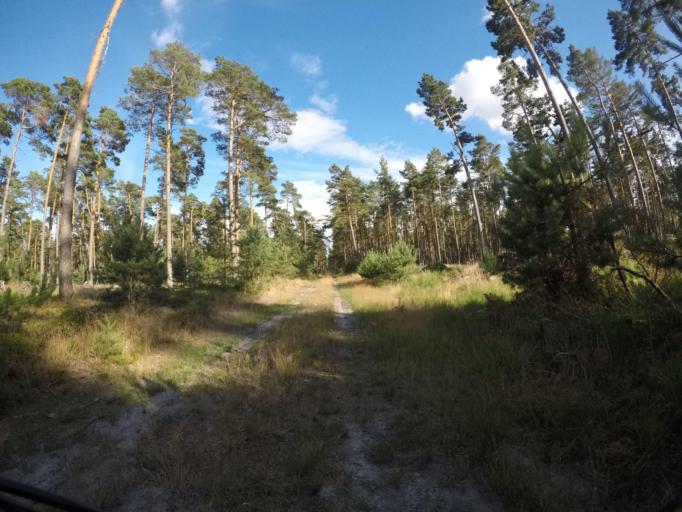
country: DE
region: Mecklenburg-Vorpommern
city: Lubtheen
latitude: 53.2554
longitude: 10.9976
